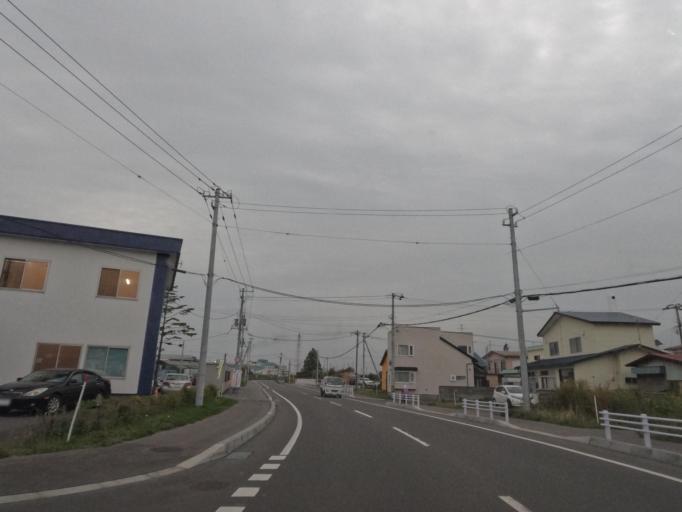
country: JP
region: Hokkaido
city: Date
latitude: 42.4750
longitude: 140.8506
